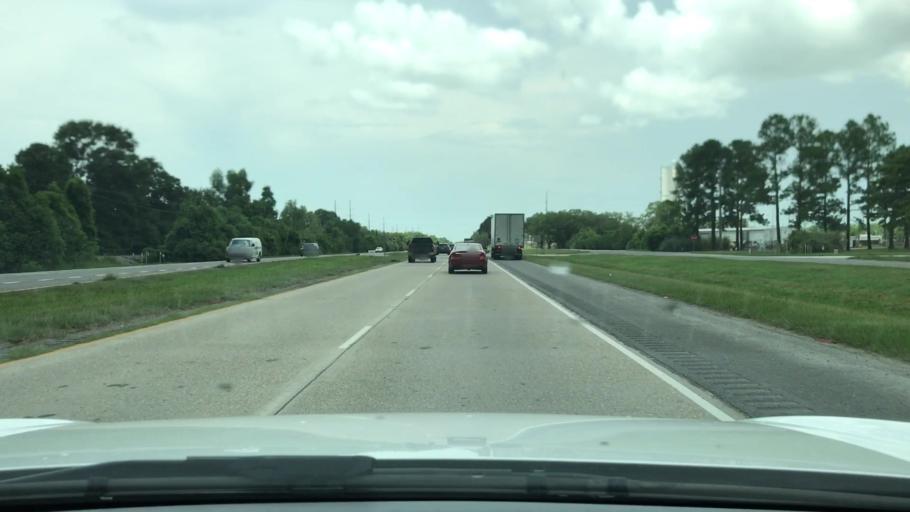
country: US
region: Louisiana
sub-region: Iberville Parish
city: Plaquemine
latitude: 30.3190
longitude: -91.2509
